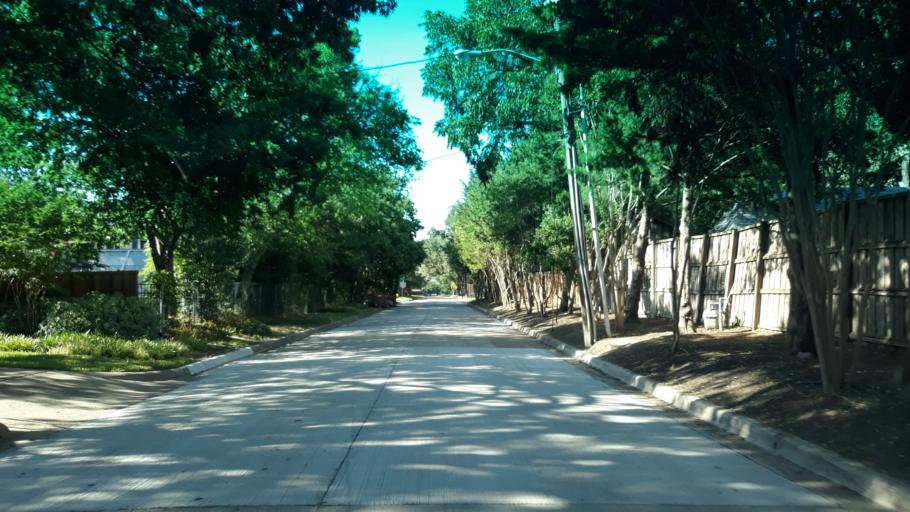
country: US
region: Texas
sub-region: Dallas County
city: Highland Park
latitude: 32.8273
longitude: -96.7560
